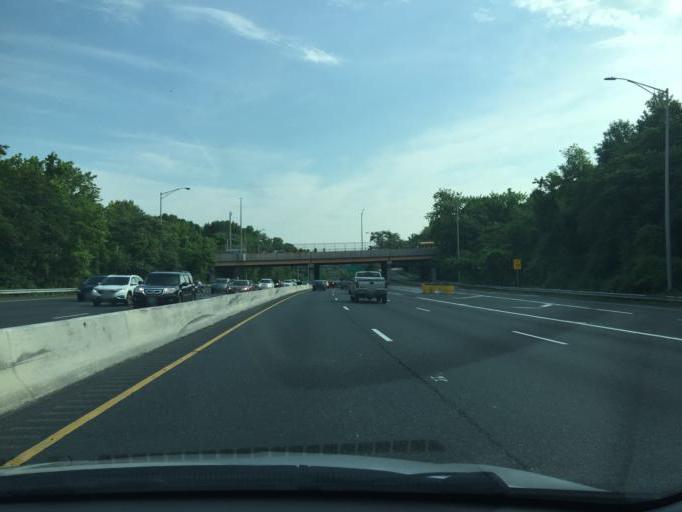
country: US
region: Maryland
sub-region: City of Baltimore
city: Baltimore
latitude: 39.3440
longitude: -76.6475
